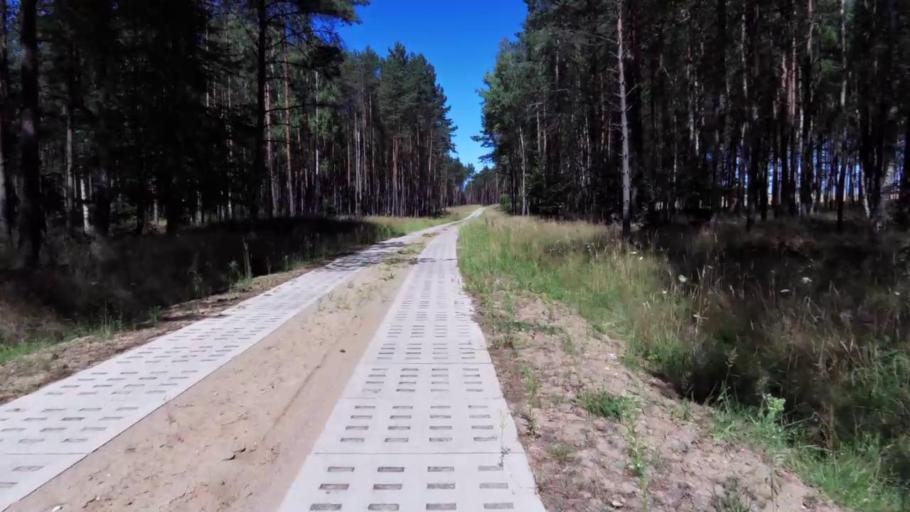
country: PL
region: West Pomeranian Voivodeship
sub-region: Powiat szczecinecki
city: Szczecinek
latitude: 53.6169
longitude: 16.6637
